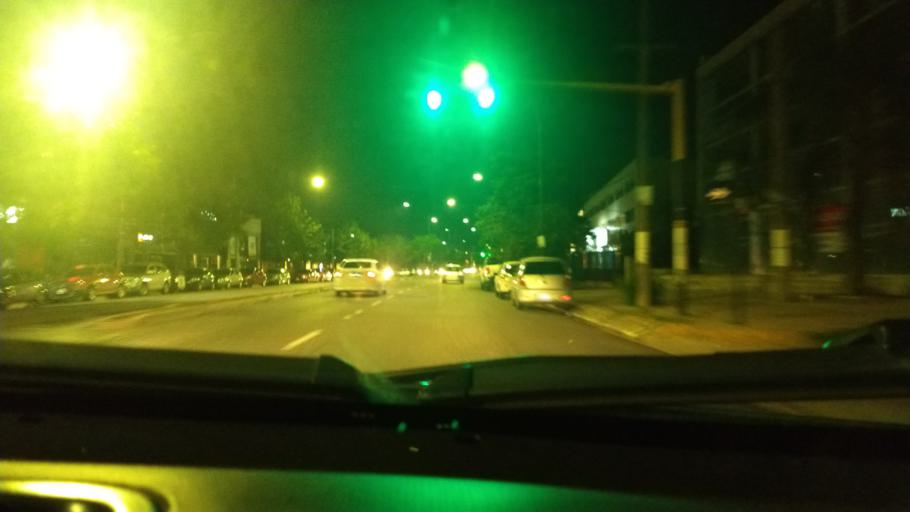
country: AR
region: Cordoba
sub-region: Departamento de Capital
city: Cordoba
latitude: -31.3628
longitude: -64.2370
